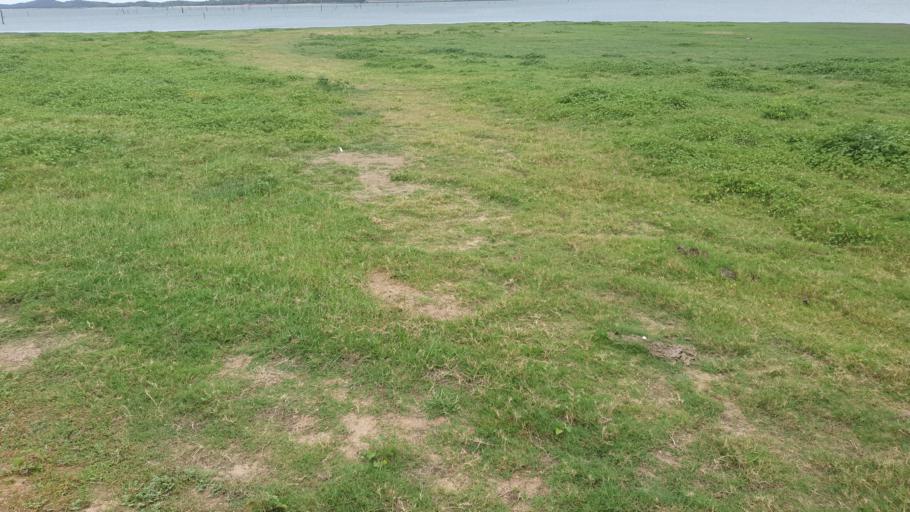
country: LK
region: North Central
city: Polonnaruwa
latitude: 8.1309
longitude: 80.9128
